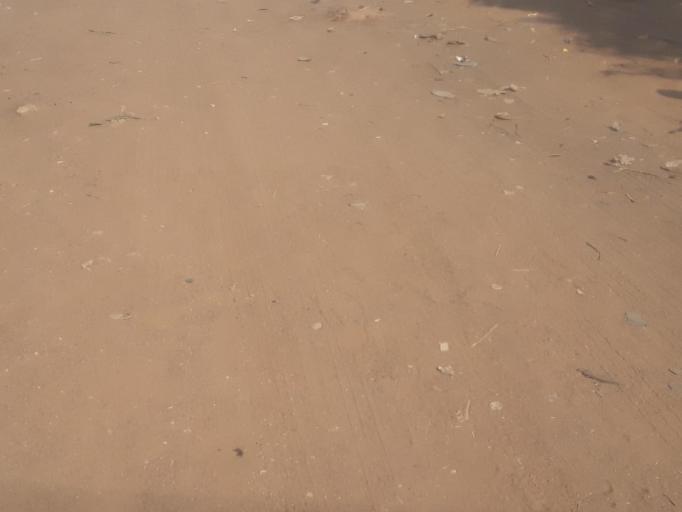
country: ZM
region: Lusaka
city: Lusaka
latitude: -15.3548
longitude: 28.2942
